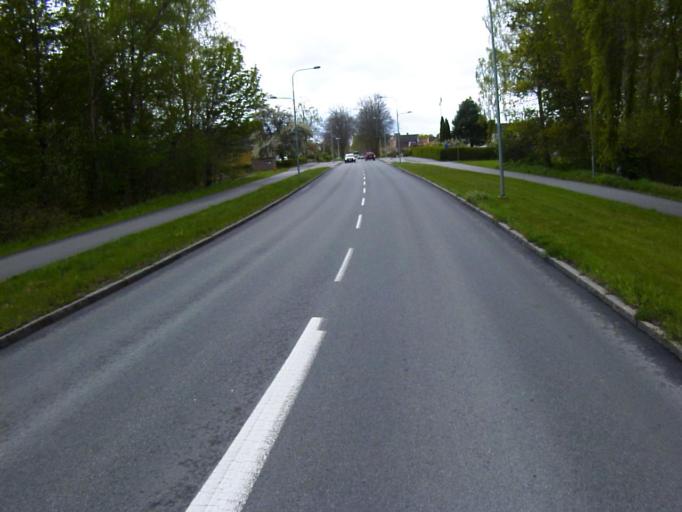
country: SE
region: Skane
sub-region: Kristianstads Kommun
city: Kristianstad
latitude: 56.0403
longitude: 14.1731
